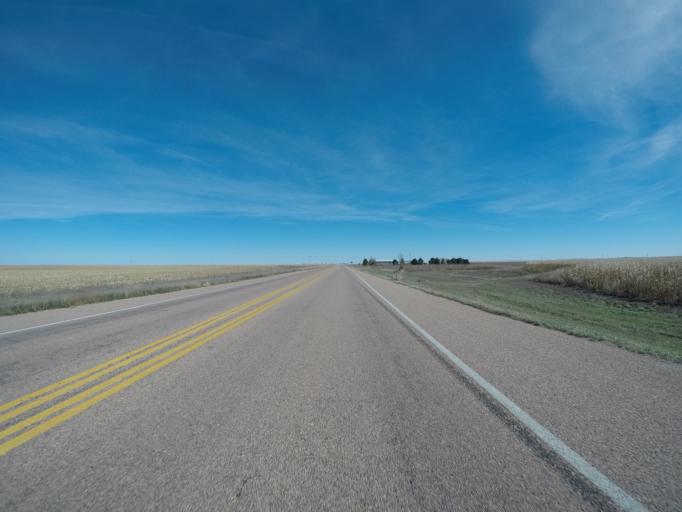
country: US
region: Colorado
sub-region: Kit Carson County
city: Burlington
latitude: 39.6563
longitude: -102.5962
